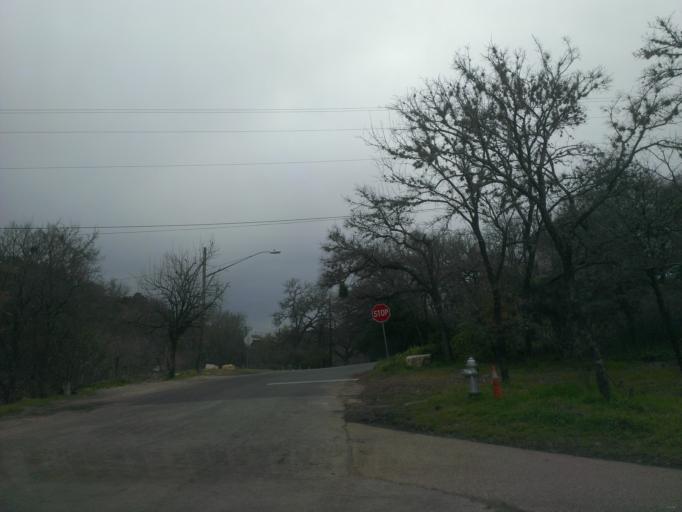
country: US
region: Texas
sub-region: Travis County
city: Austin
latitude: 30.2927
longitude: -97.7476
